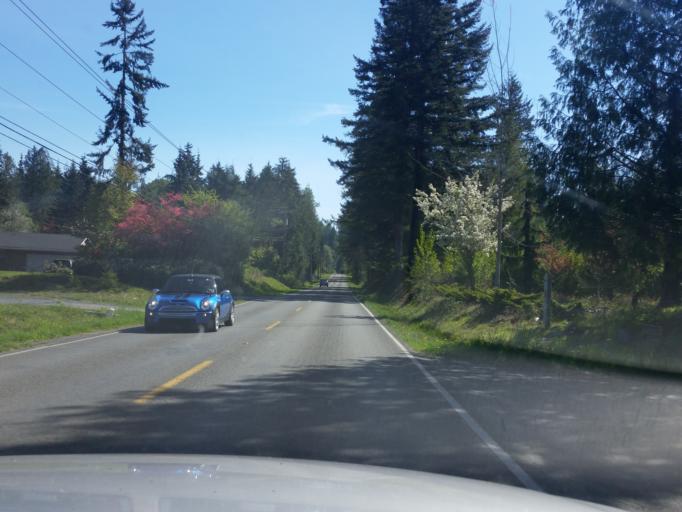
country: US
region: Washington
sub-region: Snohomish County
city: Machias
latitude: 47.9633
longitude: -122.0286
